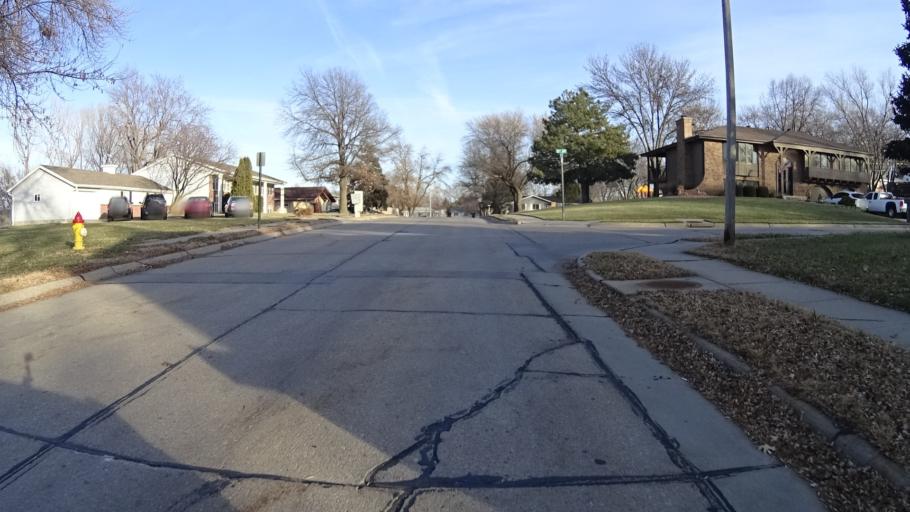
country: US
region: Nebraska
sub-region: Douglas County
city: Ralston
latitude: 41.1940
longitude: -96.0464
